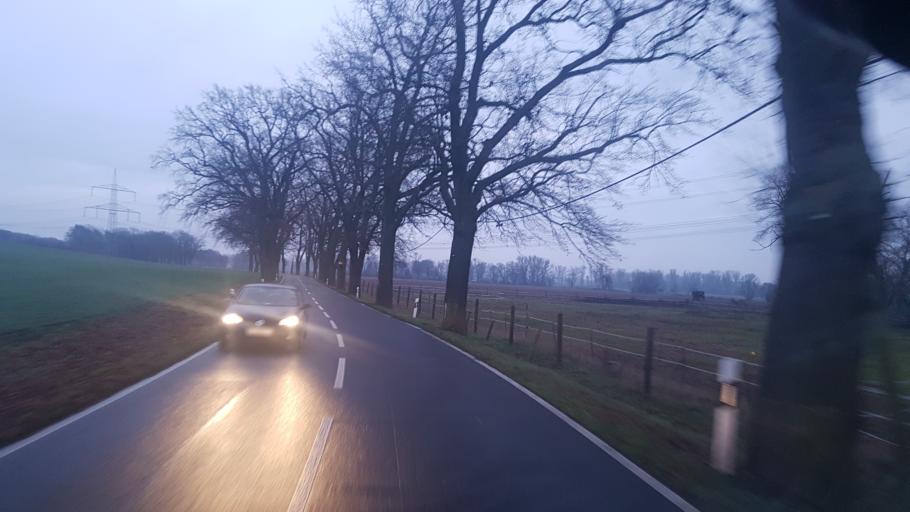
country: DE
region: Brandenburg
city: Trebbin
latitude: 52.2473
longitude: 13.2117
